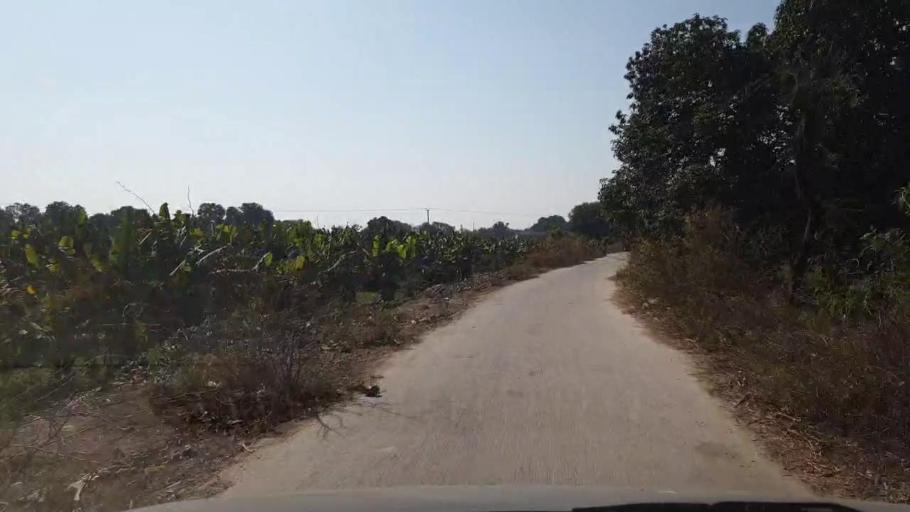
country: PK
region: Sindh
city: Tando Jam
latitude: 25.4469
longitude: 68.6243
